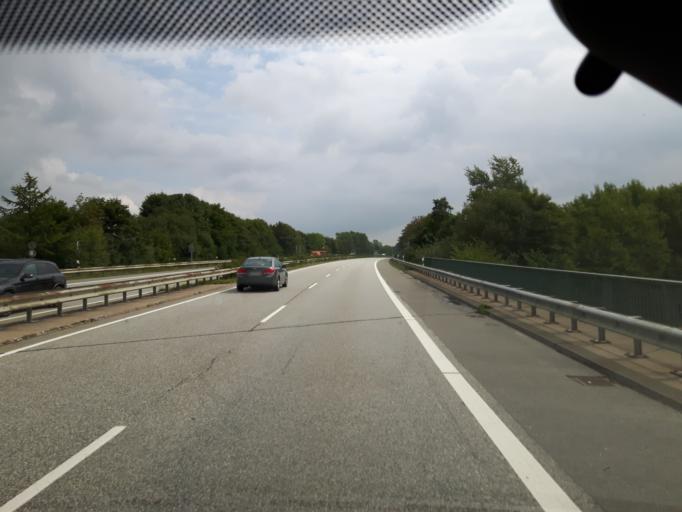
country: DE
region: Schleswig-Holstein
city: Harrislee
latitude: 54.7776
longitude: 9.3841
